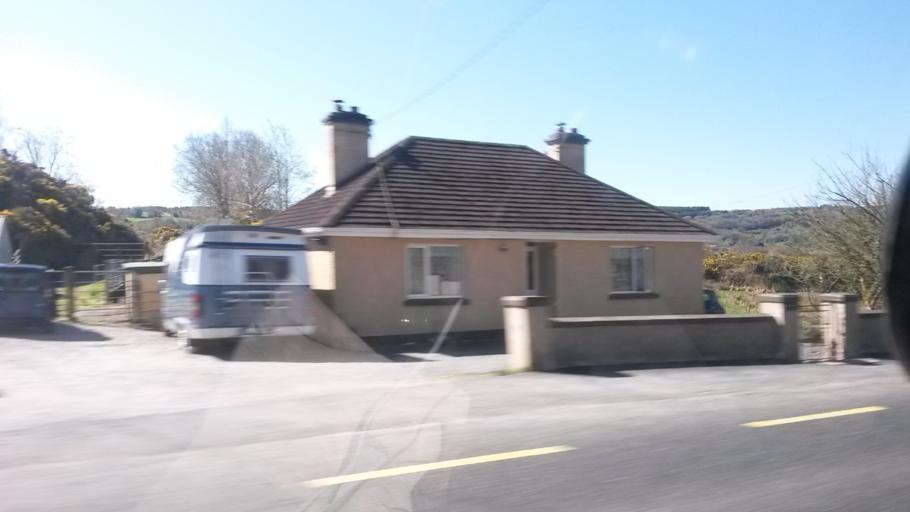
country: IE
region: Munster
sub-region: County Cork
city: Macroom
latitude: 51.9110
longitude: -9.0394
